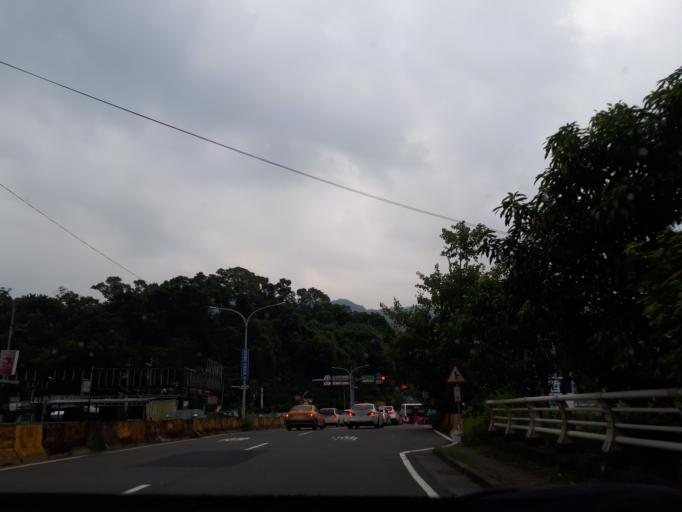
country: TW
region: Taipei
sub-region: Taipei
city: Banqiao
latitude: 24.9588
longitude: 121.5048
